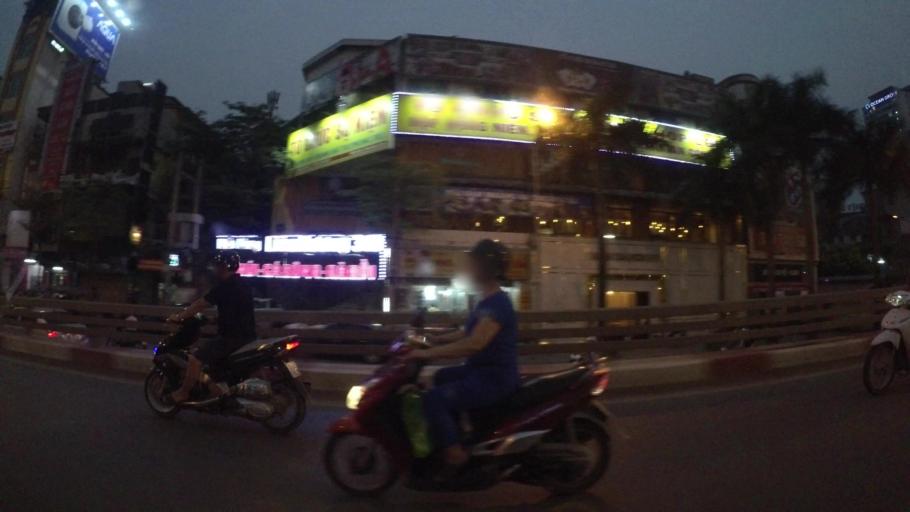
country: VN
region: Ha Noi
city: Dong Da
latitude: 21.0038
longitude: 105.8214
